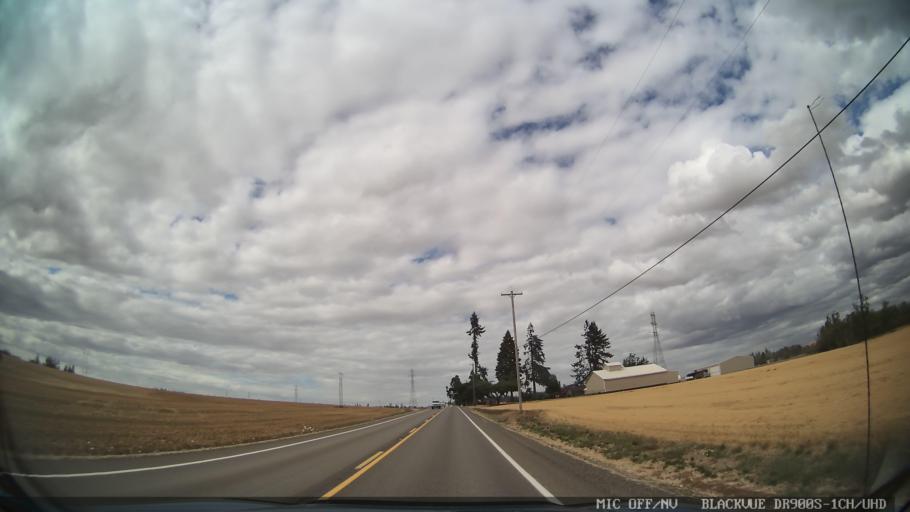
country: US
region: Oregon
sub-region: Marion County
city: Sublimity
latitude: 44.8619
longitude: -122.7926
